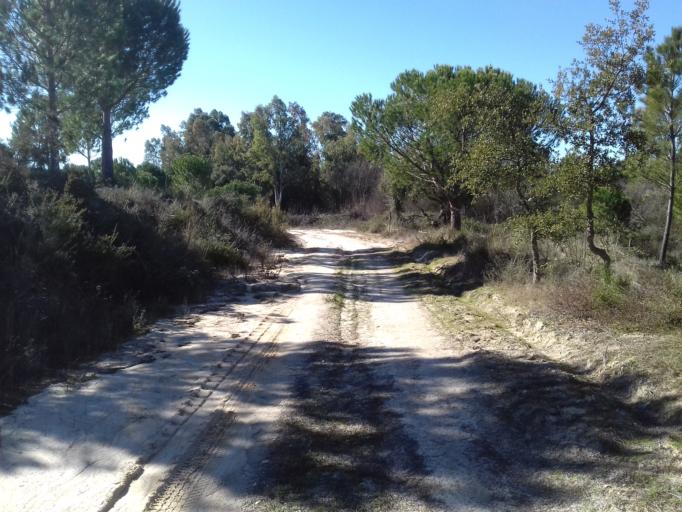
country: PT
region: Santarem
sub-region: Coruche
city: Coruche
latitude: 39.0178
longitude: -8.5546
